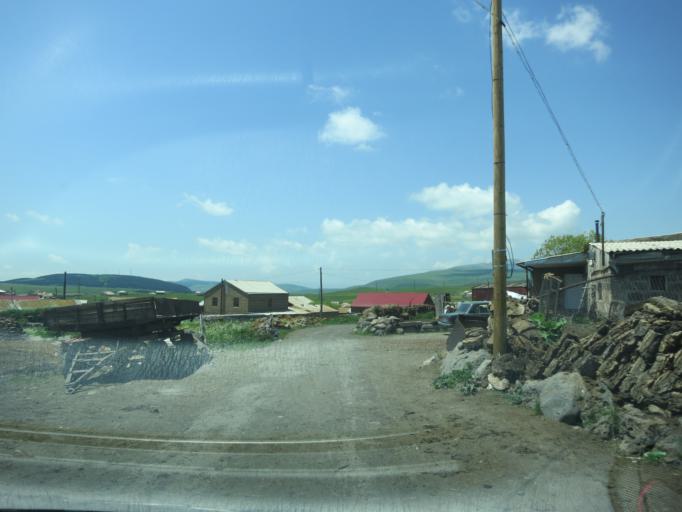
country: GE
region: Samtskhe-Javakheti
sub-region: Ninotsminda
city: Ninotsminda
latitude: 41.3973
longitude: 43.7947
